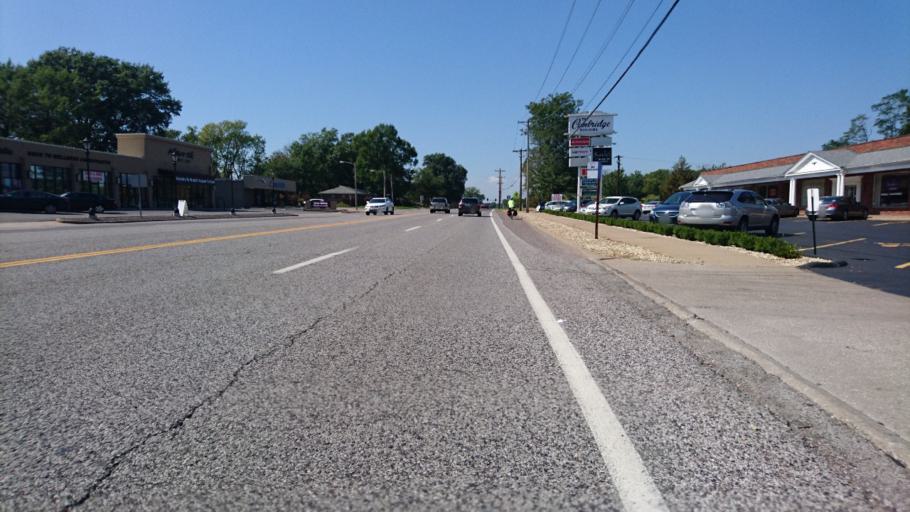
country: US
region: Missouri
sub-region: Saint Louis County
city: Des Peres
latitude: 38.5989
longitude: -90.4164
